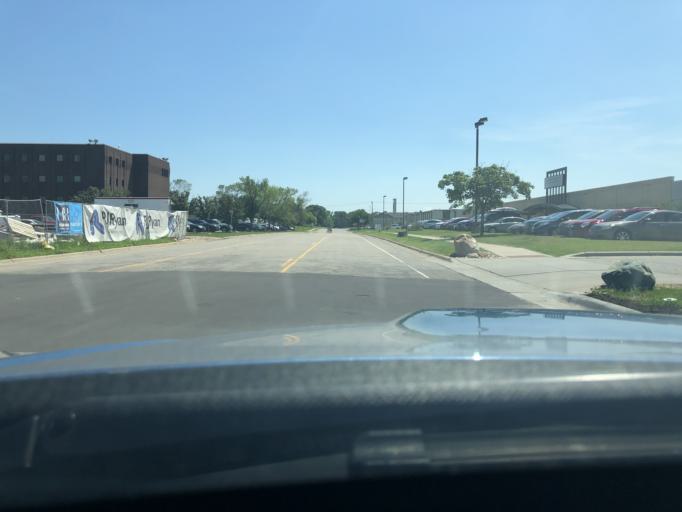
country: US
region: Minnesota
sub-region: Ramsey County
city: Roseville
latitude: 45.0168
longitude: -93.1823
